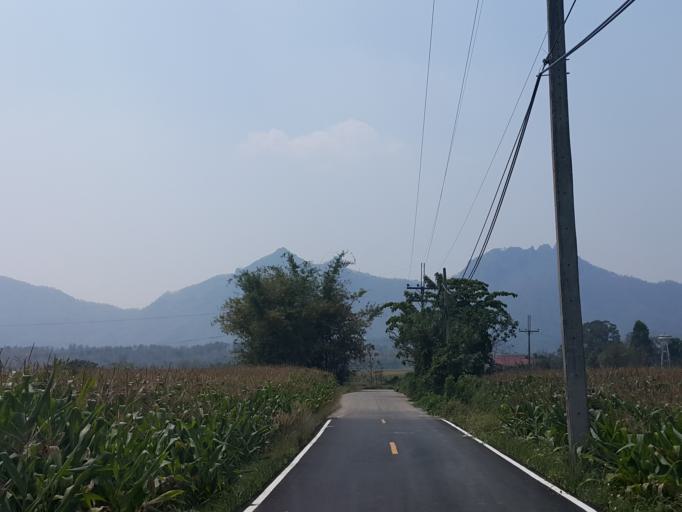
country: TH
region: Lampang
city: Chae Hom
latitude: 18.7439
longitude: 99.5721
